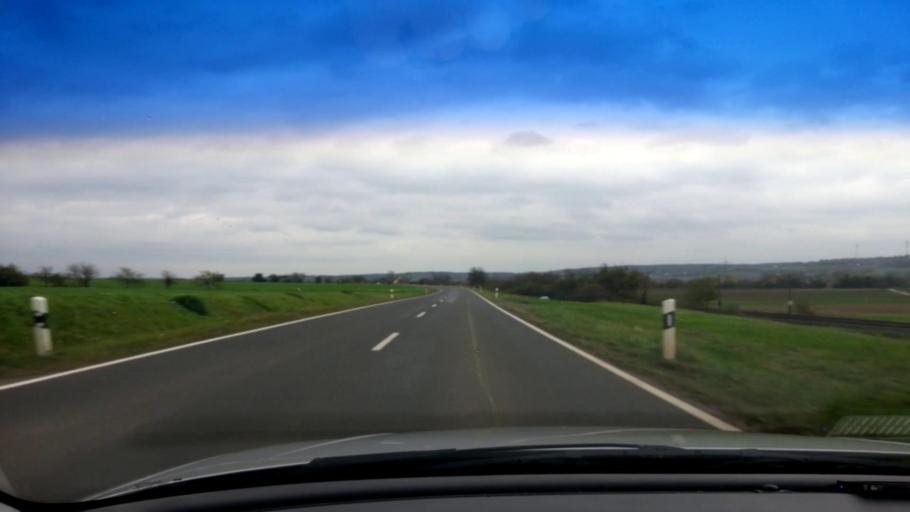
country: DE
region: Bavaria
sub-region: Regierungsbezirk Unterfranken
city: Stettfeld
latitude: 49.9561
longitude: 10.7379
